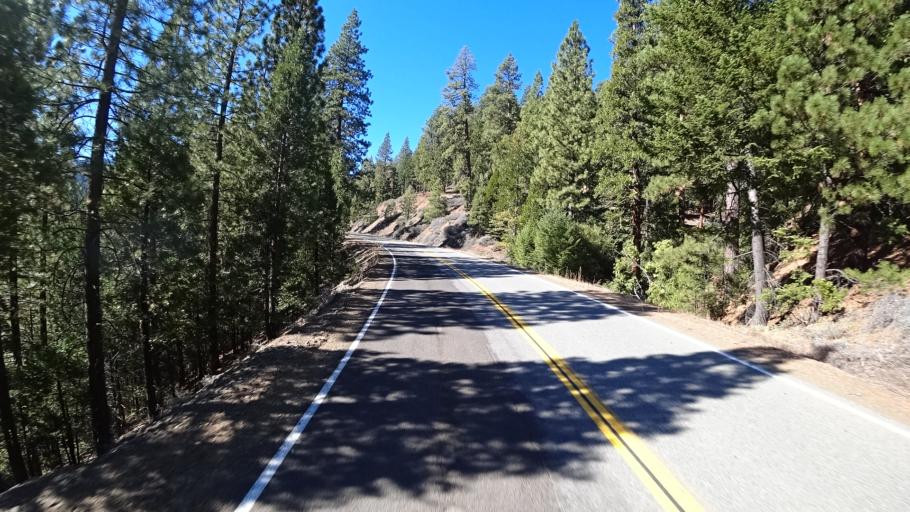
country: US
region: California
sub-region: Siskiyou County
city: Weed
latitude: 41.2727
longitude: -122.8753
